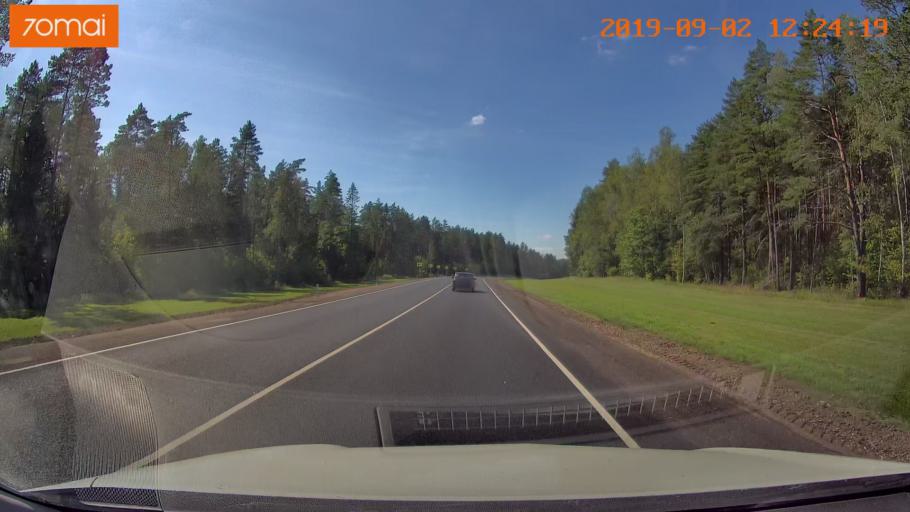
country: RU
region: Smolensk
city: Shumyachi
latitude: 53.8692
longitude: 32.6102
